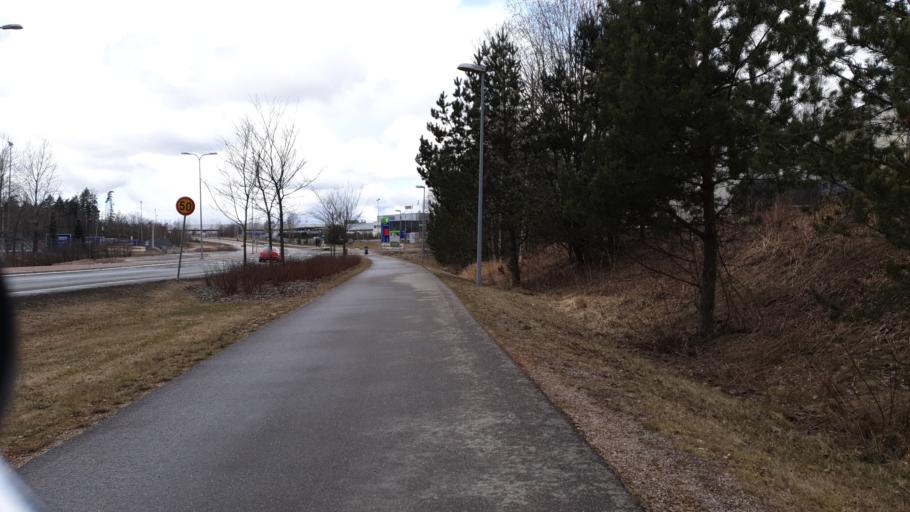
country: FI
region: Uusimaa
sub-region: Helsinki
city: Vantaa
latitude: 60.2943
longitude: 24.9257
